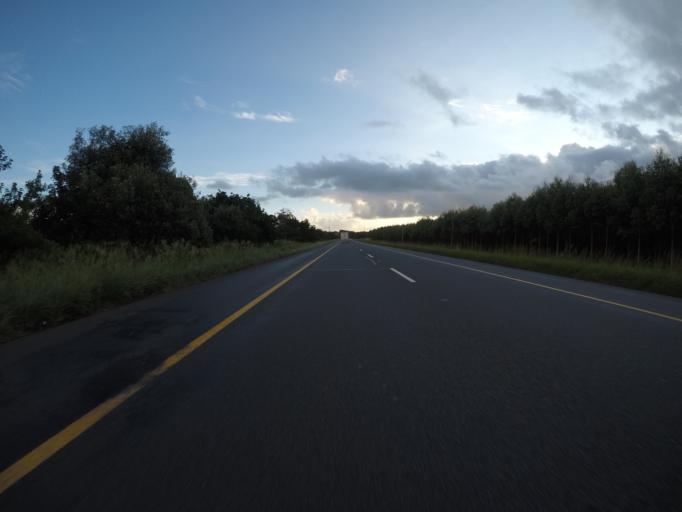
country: ZA
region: KwaZulu-Natal
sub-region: uThungulu District Municipality
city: KwaMbonambi
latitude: -28.5726
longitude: 32.1087
